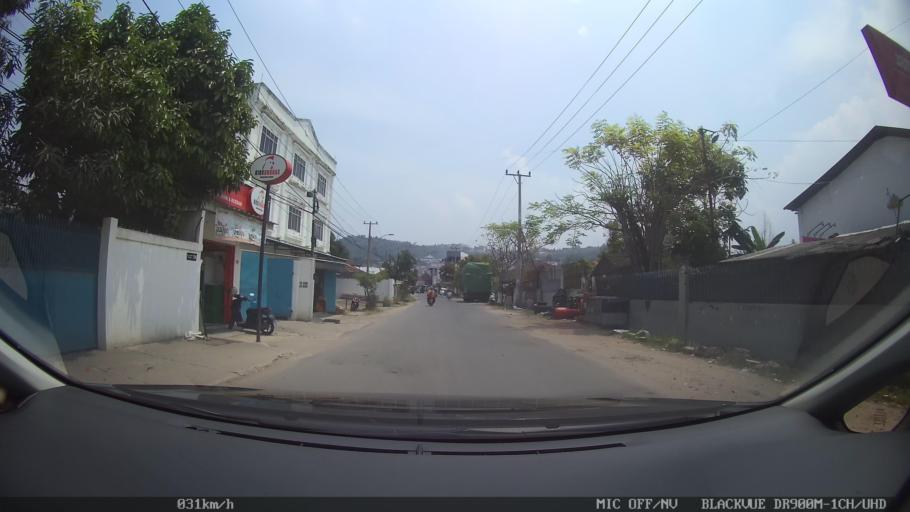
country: ID
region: Lampung
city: Bandarlampung
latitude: -5.4426
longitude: 105.2839
